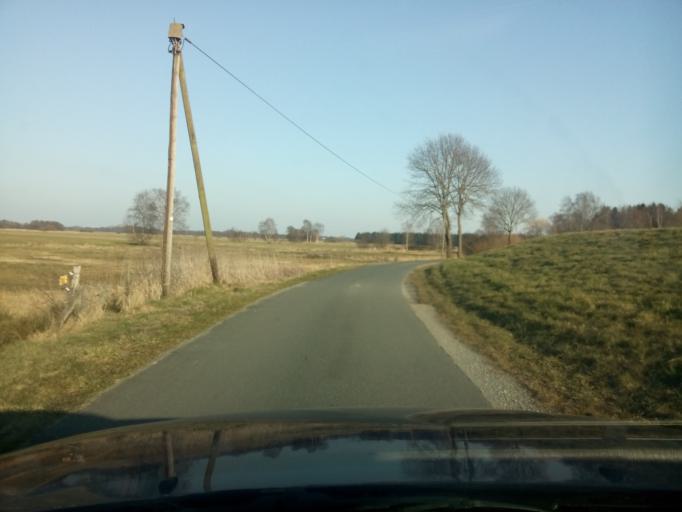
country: DE
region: Lower Saxony
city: Lilienthal
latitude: 53.1444
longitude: 8.8519
